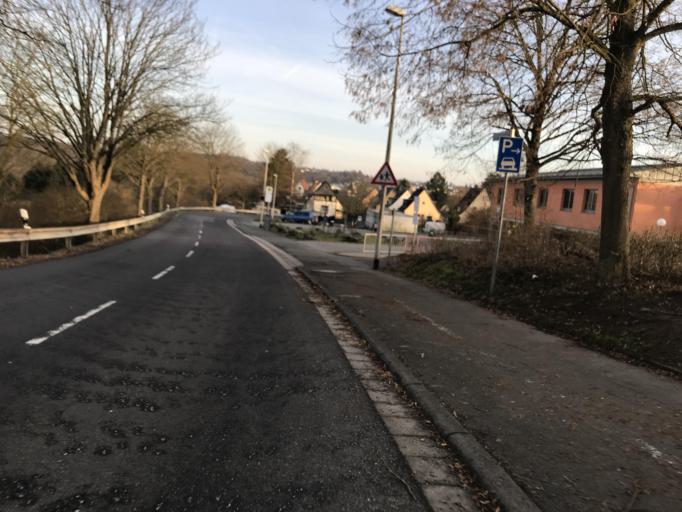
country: DE
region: Hesse
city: Weilburg
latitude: 50.4937
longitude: 8.2623
